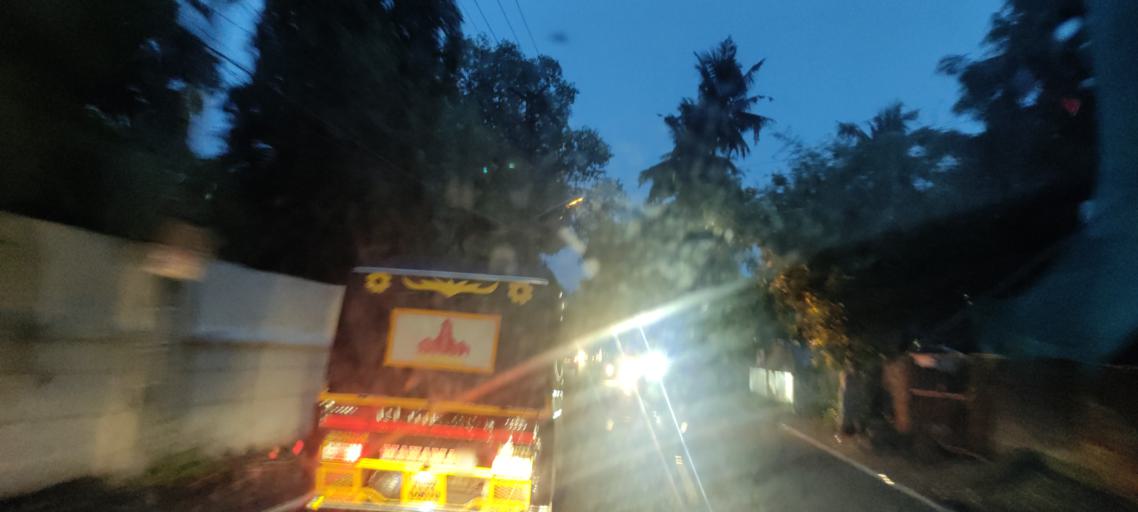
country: IN
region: Kerala
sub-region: Ernakulam
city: Cochin
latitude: 9.8990
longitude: 76.2953
